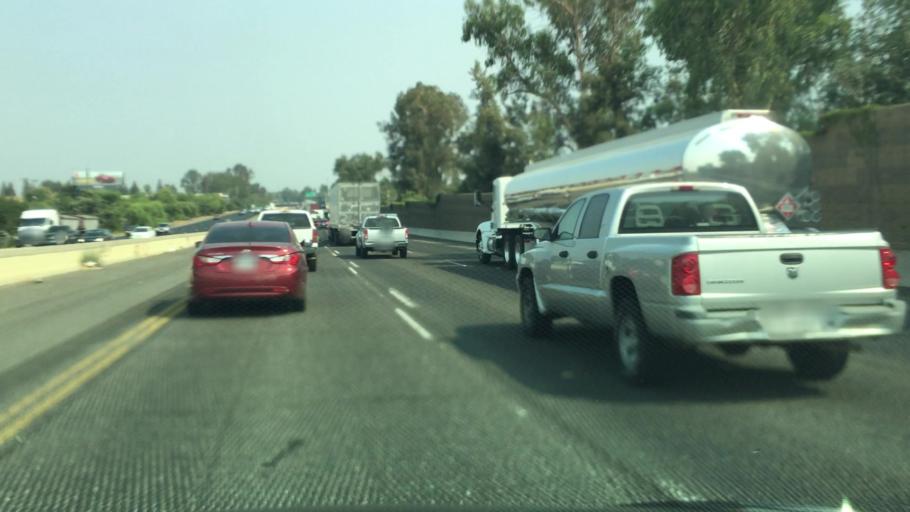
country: US
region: California
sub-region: Fresno County
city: West Park
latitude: 36.7992
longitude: -119.8739
